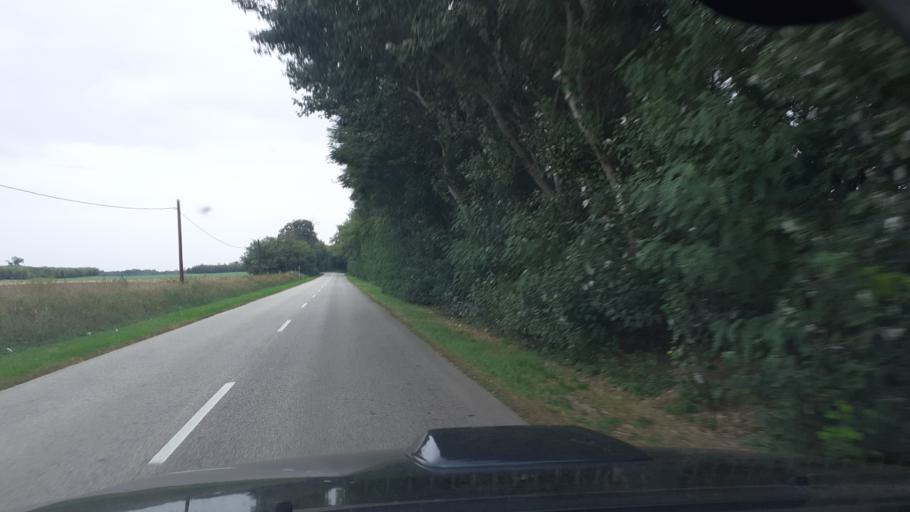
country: HU
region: Fejer
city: Baracs
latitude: 46.8427
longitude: 18.8919
